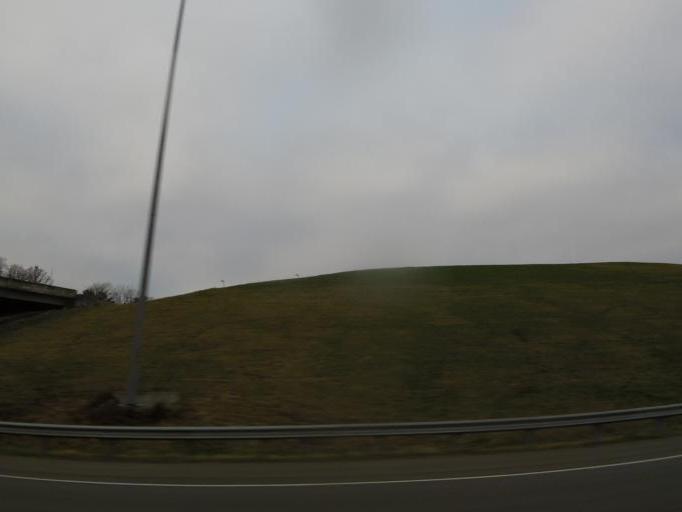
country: US
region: Alabama
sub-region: Jefferson County
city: Fultondale
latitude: 33.6091
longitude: -86.8094
